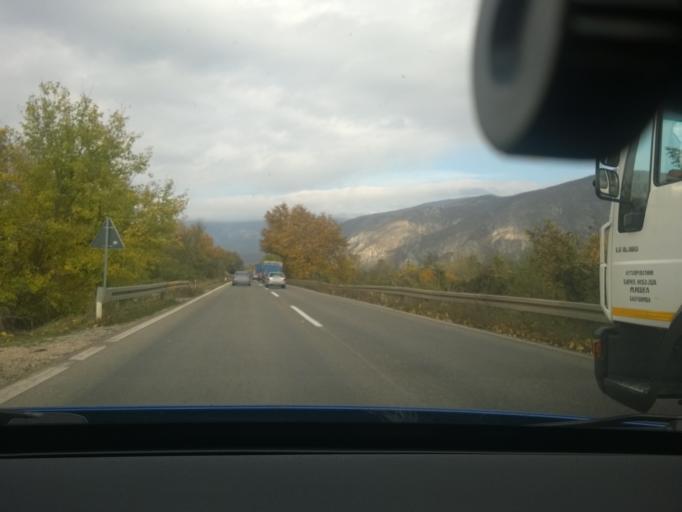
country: RS
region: Central Serbia
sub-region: Pirotski Okrug
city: Bela Palanka
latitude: 43.2811
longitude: 22.2226
